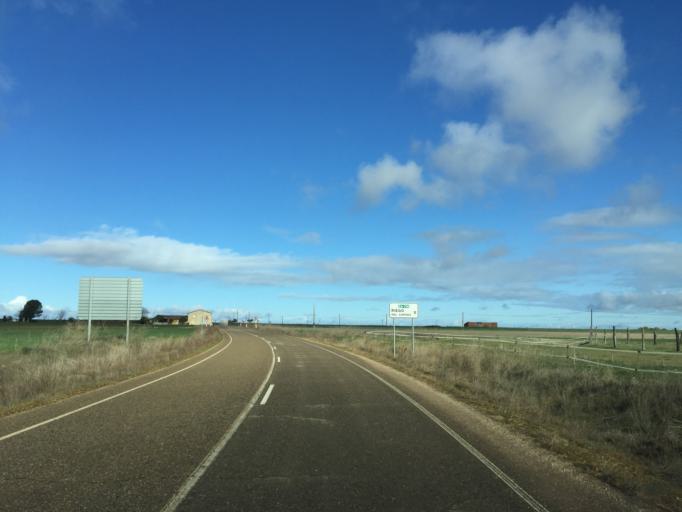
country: ES
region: Castille and Leon
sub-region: Provincia de Zamora
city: Manganeses de la Lampreana
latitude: 41.7540
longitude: -5.7160
